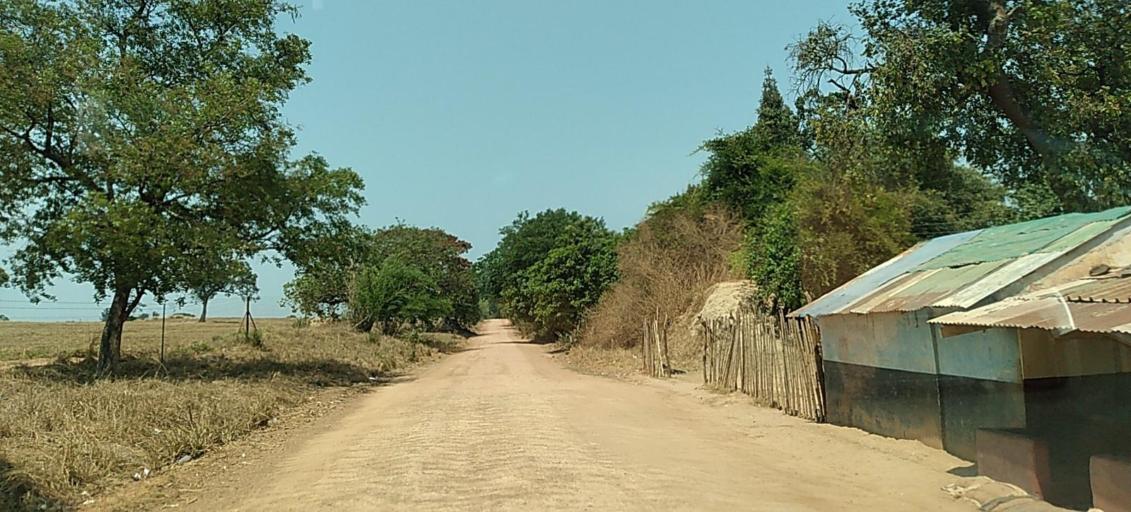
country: ZM
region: Copperbelt
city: Chambishi
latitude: -12.6242
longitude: 27.9513
